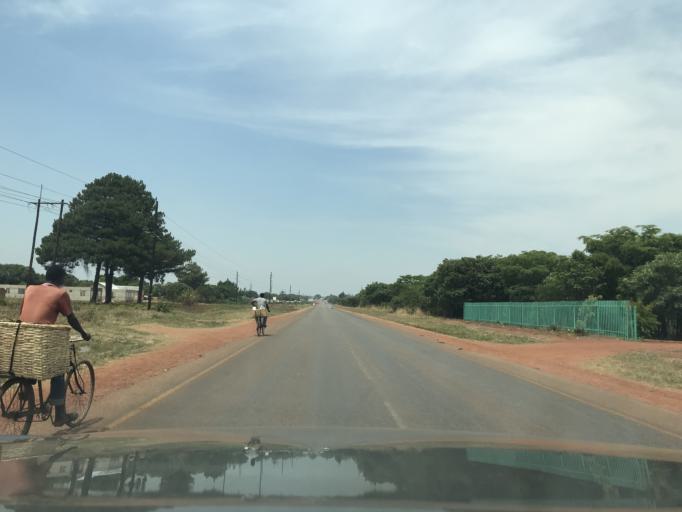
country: ZM
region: Northern
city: Kasama
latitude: -10.2115
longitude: 31.1616
